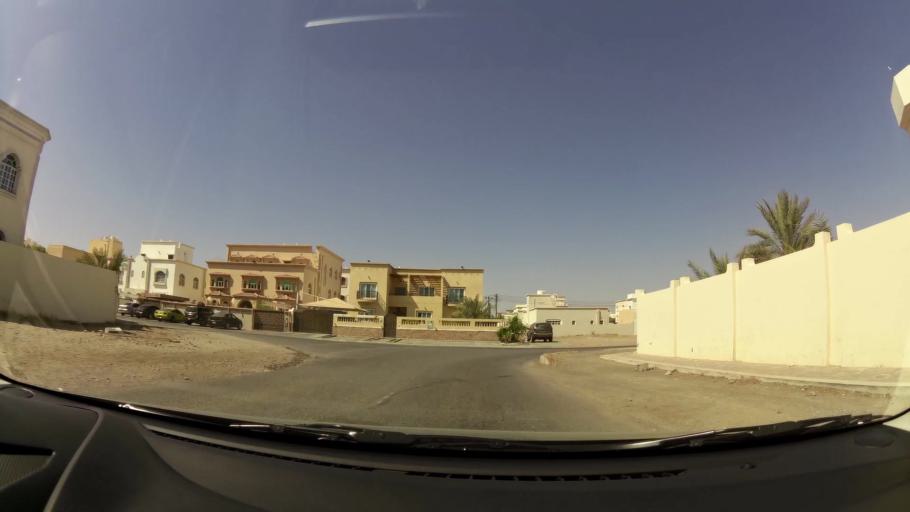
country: OM
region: Muhafazat Masqat
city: As Sib al Jadidah
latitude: 23.6079
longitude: 58.2413
